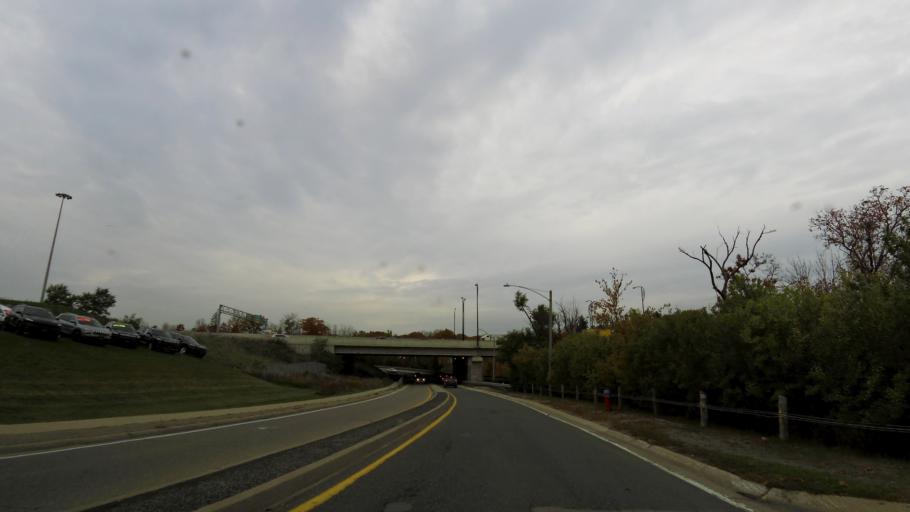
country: CA
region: Ontario
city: Oakville
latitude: 43.4507
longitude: -79.6935
